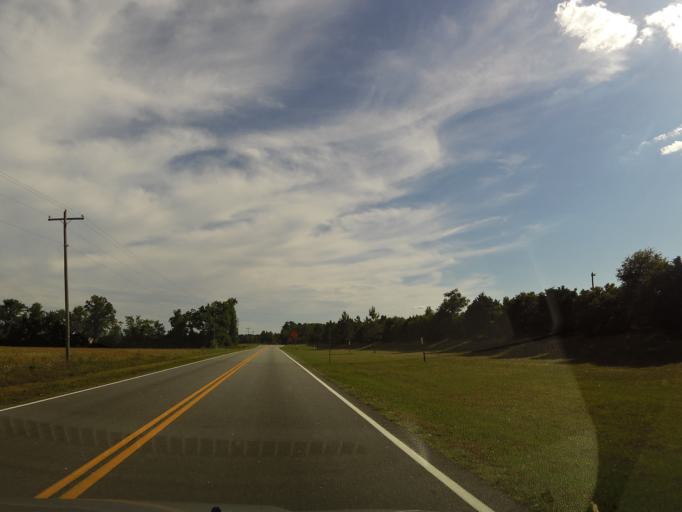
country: US
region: South Carolina
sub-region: Allendale County
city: Fairfax
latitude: 32.9920
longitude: -81.2229
